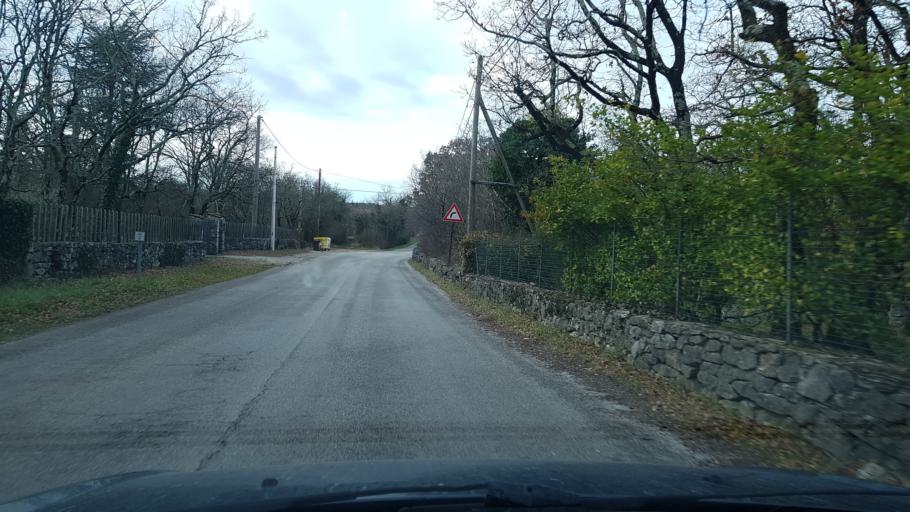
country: IT
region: Friuli Venezia Giulia
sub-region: Provincia di Trieste
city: Sgonico
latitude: 45.7292
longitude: 13.7350
